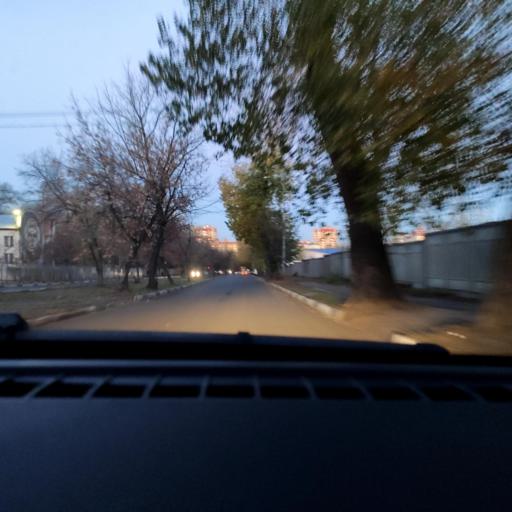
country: RU
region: Voronezj
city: Voronezh
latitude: 51.6420
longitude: 39.2450
